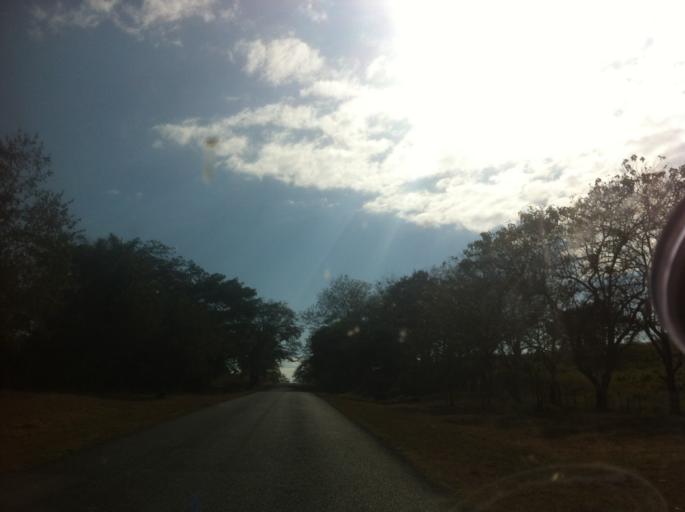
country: NI
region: Rio San Juan
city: San Miguelito
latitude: 11.4325
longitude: -84.8821
